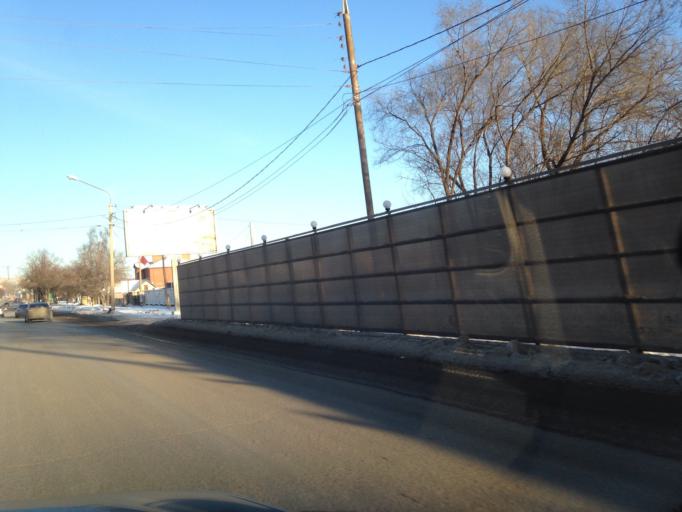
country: RU
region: Ulyanovsk
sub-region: Ulyanovskiy Rayon
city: Ulyanovsk
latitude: 54.2911
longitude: 48.3706
